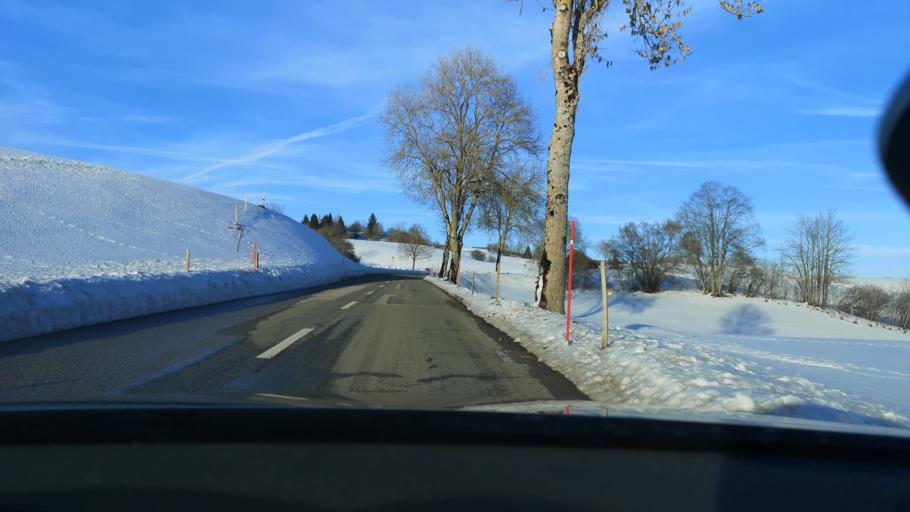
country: CH
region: Neuchatel
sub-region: Val-de-Travers District
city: Fleurier
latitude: 46.9093
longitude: 6.5006
